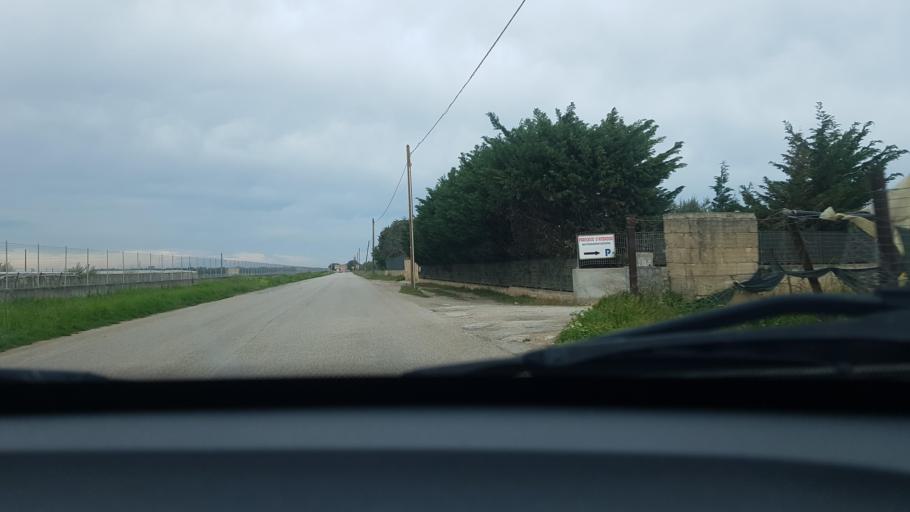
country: IT
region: Apulia
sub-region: Provincia di Bari
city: Noicattaro
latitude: 41.0358
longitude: 16.9727
